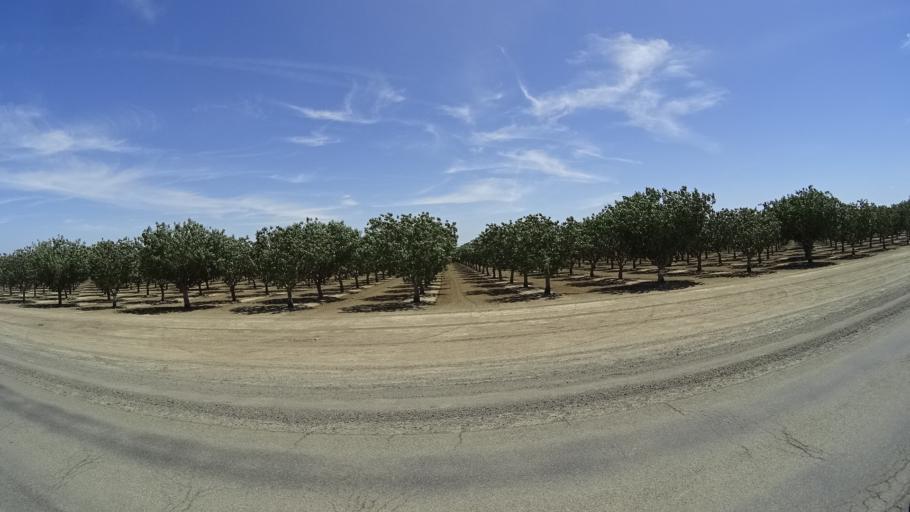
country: US
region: California
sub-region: Kings County
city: Kettleman City
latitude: 35.9241
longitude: -119.9149
